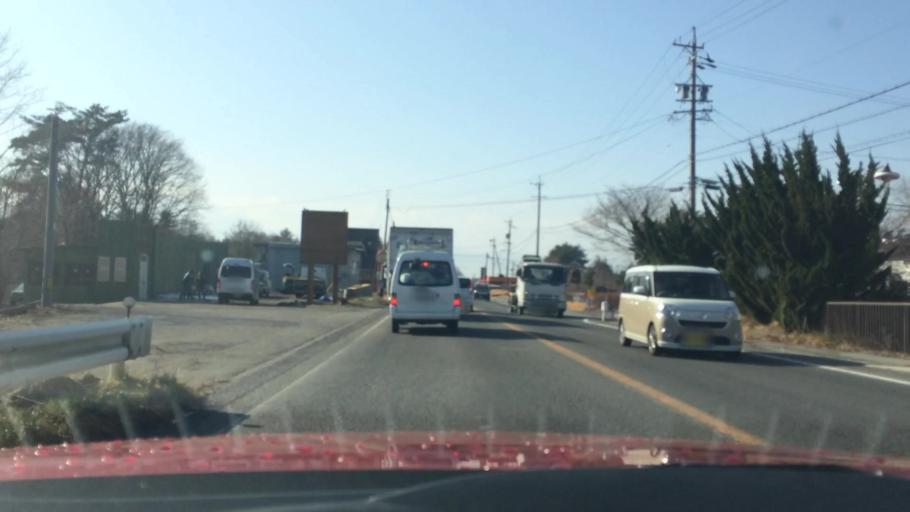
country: JP
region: Nagano
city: Komoro
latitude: 36.3303
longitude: 138.5185
